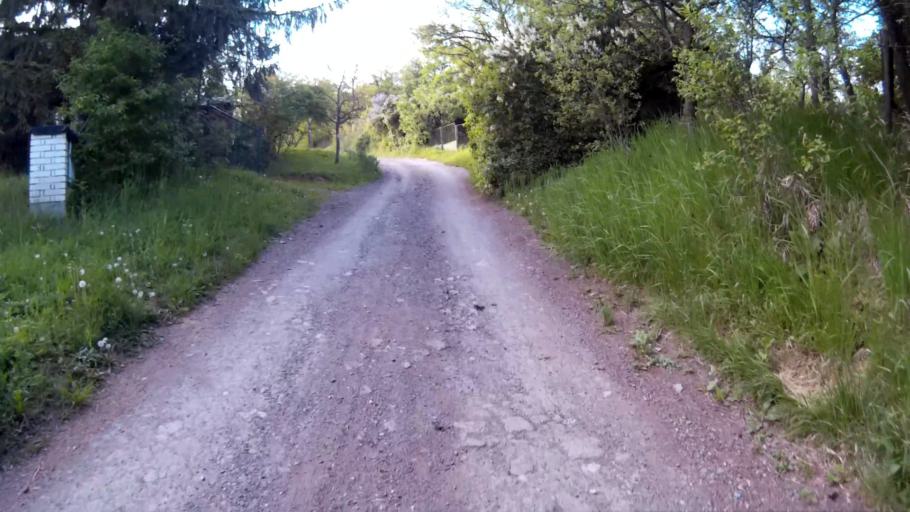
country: CZ
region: South Moravian
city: Troubsko
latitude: 49.1837
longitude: 16.5264
